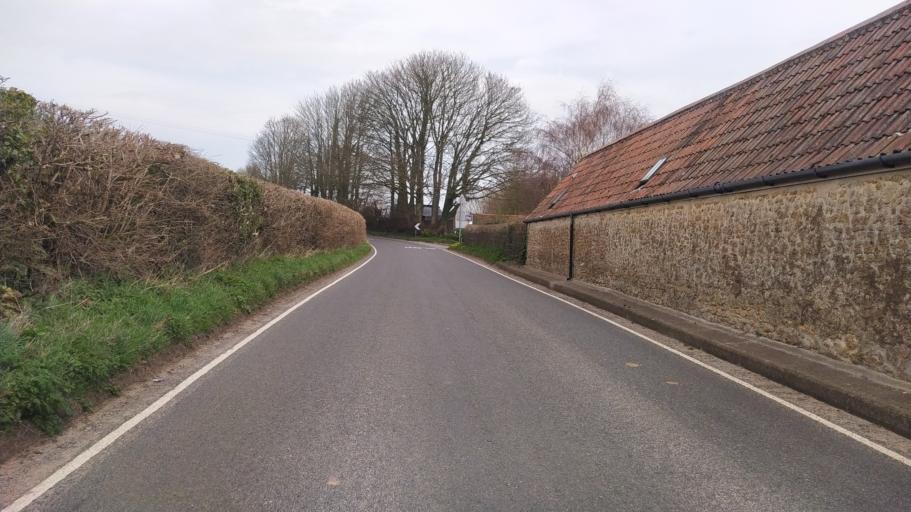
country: GB
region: England
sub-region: Somerset
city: Crewkerne
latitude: 50.8585
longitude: -2.7533
